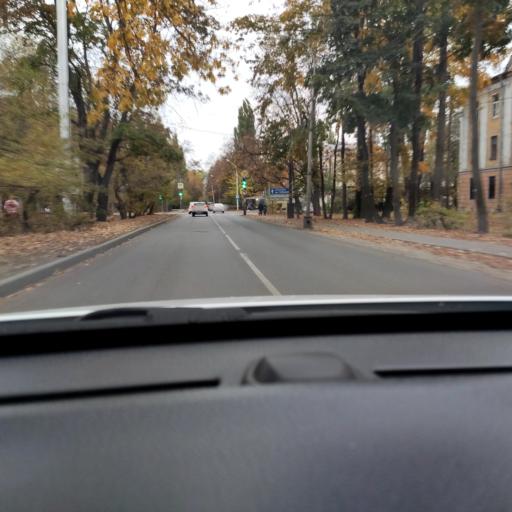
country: RU
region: Voronezj
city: Voronezh
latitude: 51.7148
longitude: 39.2231
